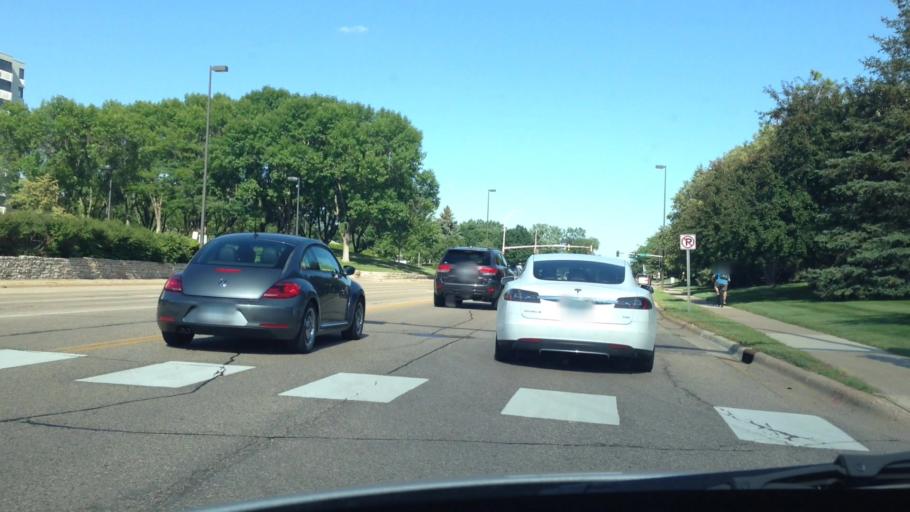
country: US
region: Minnesota
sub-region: Hennepin County
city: Bloomington
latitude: 44.8655
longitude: -93.3238
